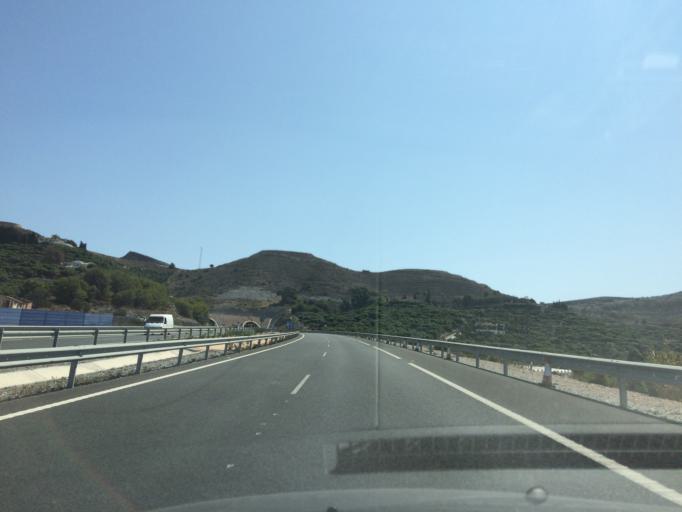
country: ES
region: Andalusia
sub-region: Provincia de Granada
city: El Varadero
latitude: 36.7195
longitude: -3.4624
